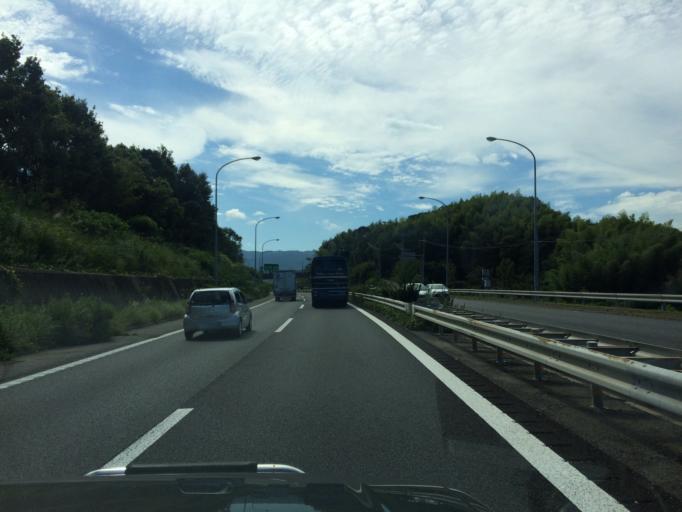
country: JP
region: Osaka
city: Izumi
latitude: 34.4437
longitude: 135.4435
